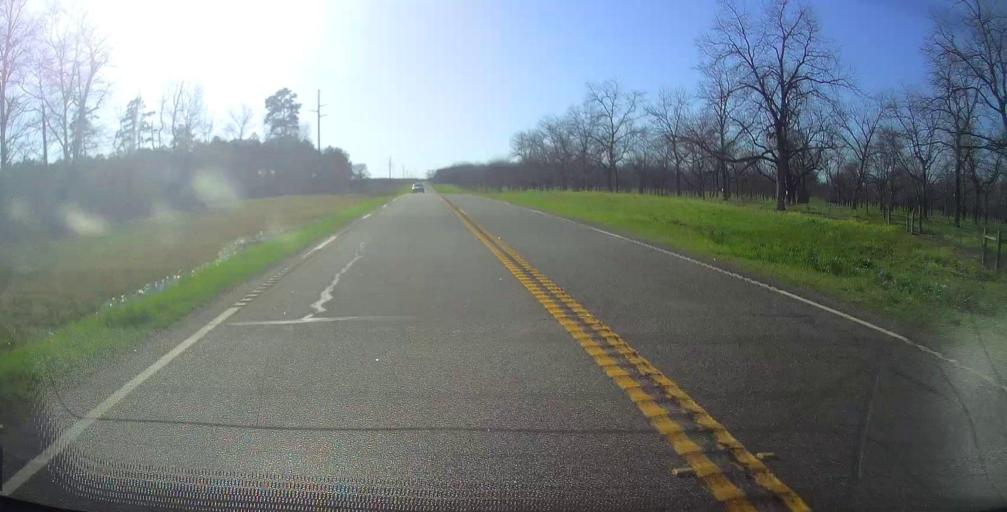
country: US
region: Georgia
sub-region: Macon County
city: Marshallville
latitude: 32.4394
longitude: -83.8558
